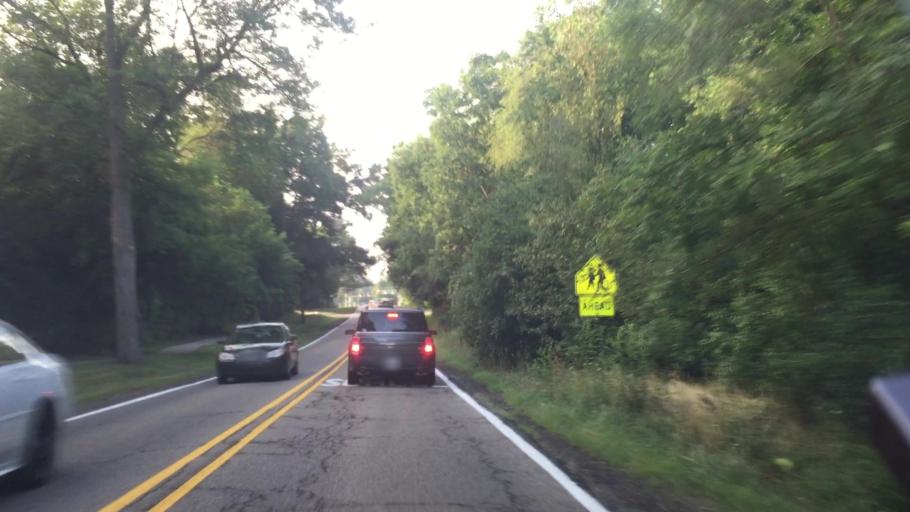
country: US
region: Michigan
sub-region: Oakland County
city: Bloomfield Hills
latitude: 42.6015
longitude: -83.2478
